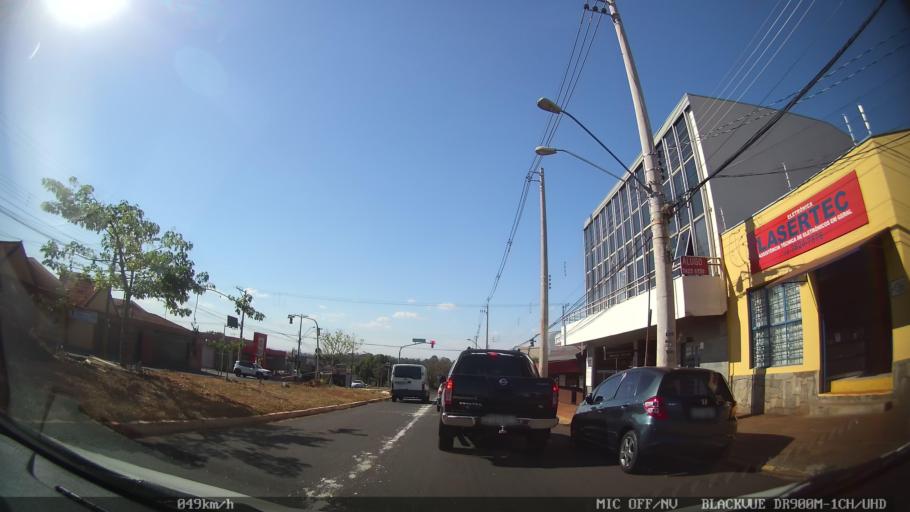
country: BR
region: Sao Paulo
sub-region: Ribeirao Preto
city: Ribeirao Preto
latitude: -21.1711
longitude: -47.7926
